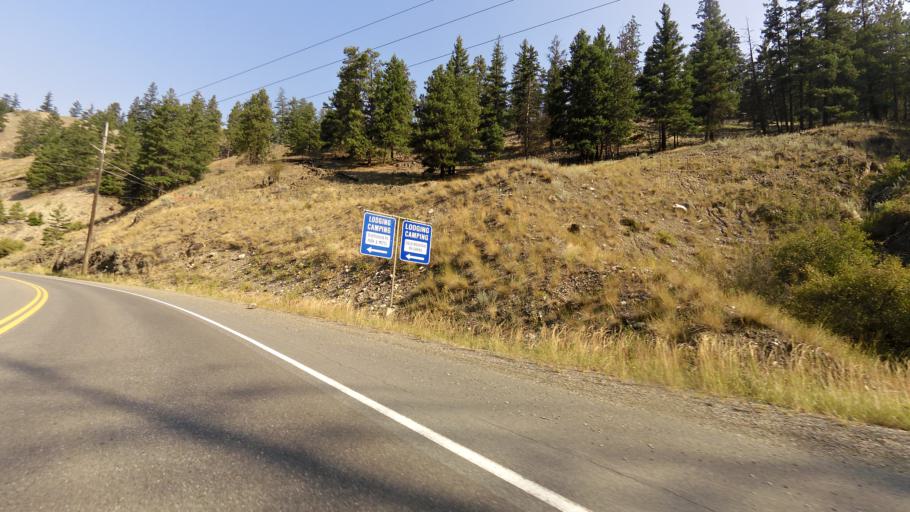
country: CA
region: British Columbia
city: Princeton
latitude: 49.3655
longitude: -120.1182
